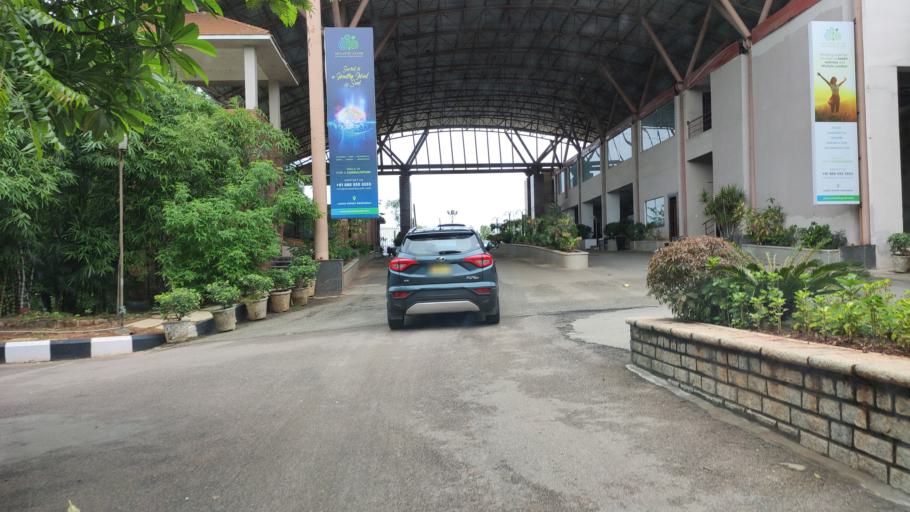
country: IN
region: Telangana
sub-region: Rangareddi
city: Secunderabad
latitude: 17.5782
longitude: 78.6016
